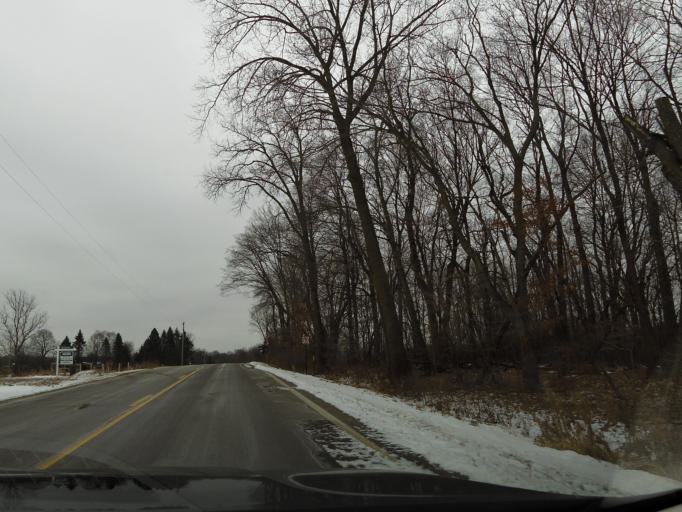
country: US
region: Minnesota
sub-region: Hennepin County
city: Medina
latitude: 45.0158
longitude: -93.6128
